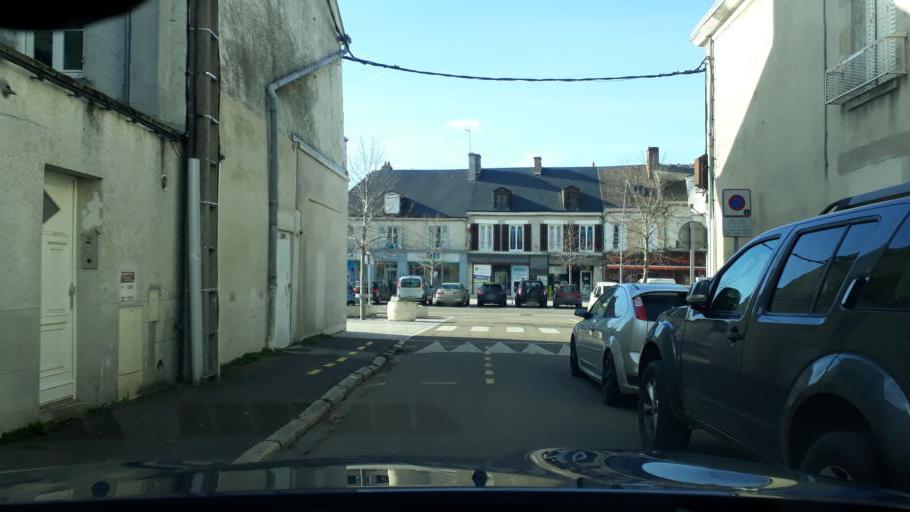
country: FR
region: Centre
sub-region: Departement du Loiret
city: Neuville-aux-Bois
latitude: 48.0694
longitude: 2.0538
